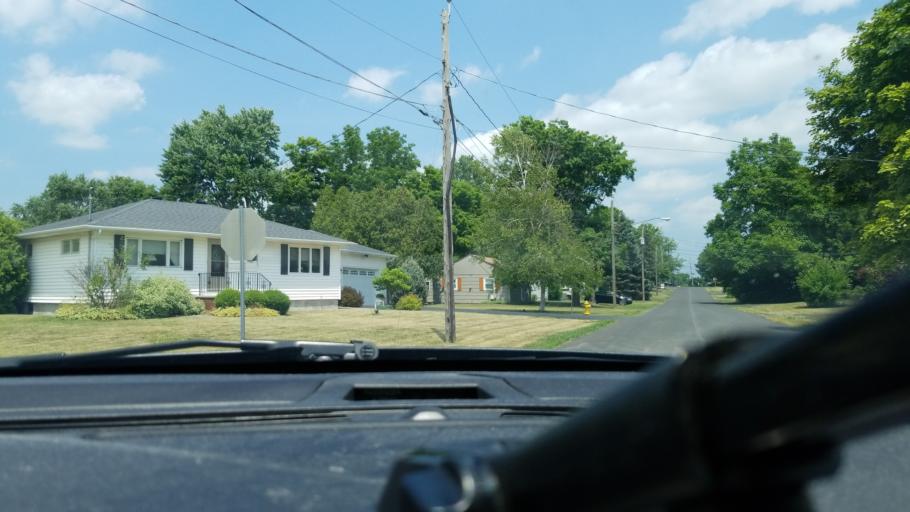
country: US
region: New York
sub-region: Onondaga County
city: Galeville
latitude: 43.0917
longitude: -76.1755
